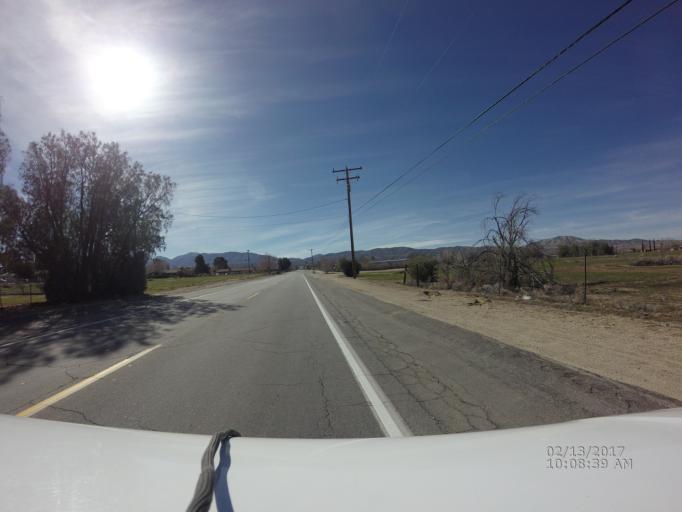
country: US
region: California
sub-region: Los Angeles County
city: Littlerock
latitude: 34.5313
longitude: -117.9749
